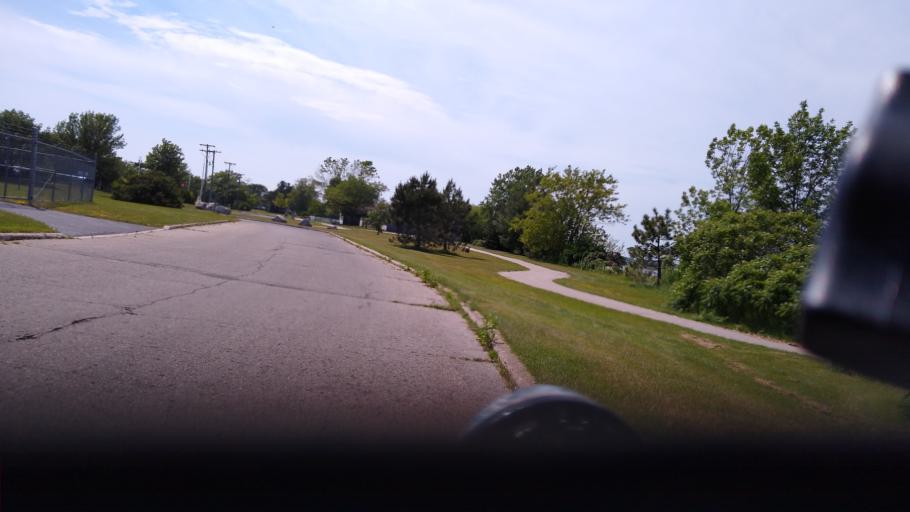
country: US
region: Michigan
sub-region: Delta County
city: Escanaba
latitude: 45.7445
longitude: -87.0415
